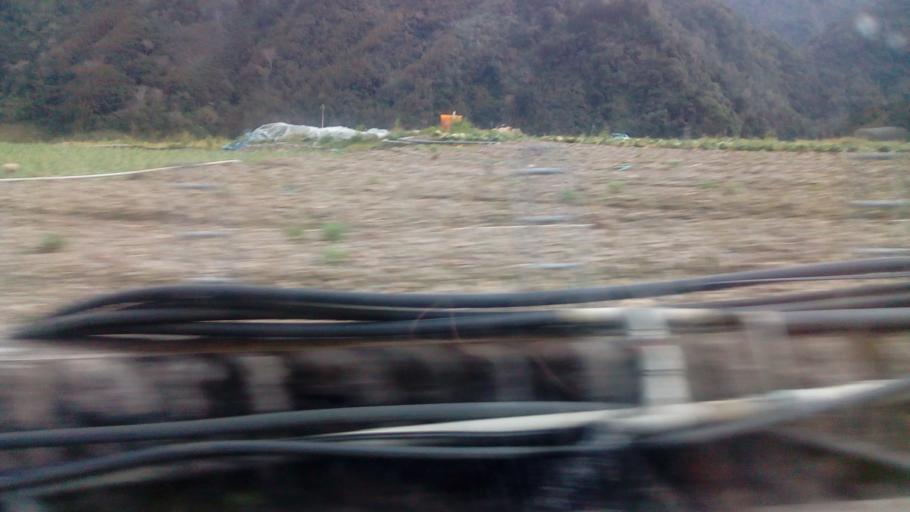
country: TW
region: Taiwan
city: Daxi
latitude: 24.4704
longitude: 121.4084
